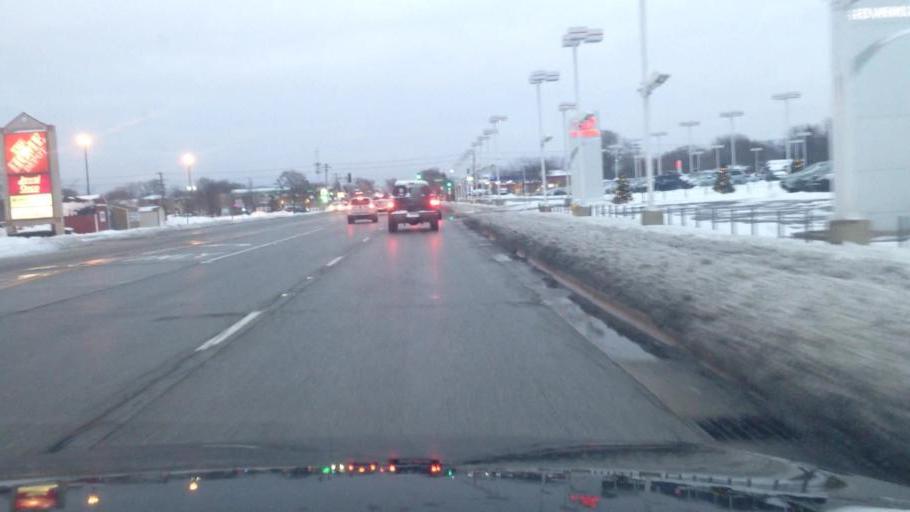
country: US
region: Illinois
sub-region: Cook County
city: Park Ridge
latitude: 42.0399
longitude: -87.8432
